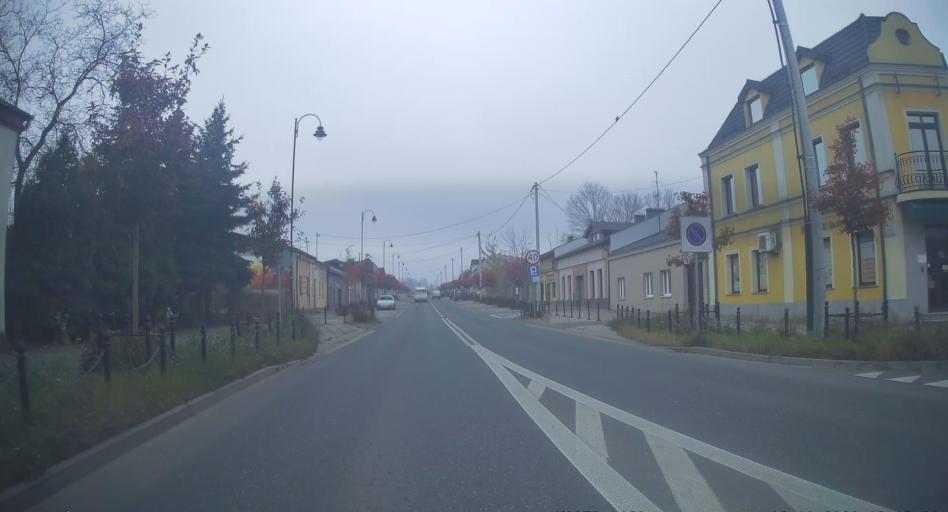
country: PL
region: Silesian Voivodeship
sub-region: Czestochowa
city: Czestochowa
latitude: 50.8165
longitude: 19.0942
